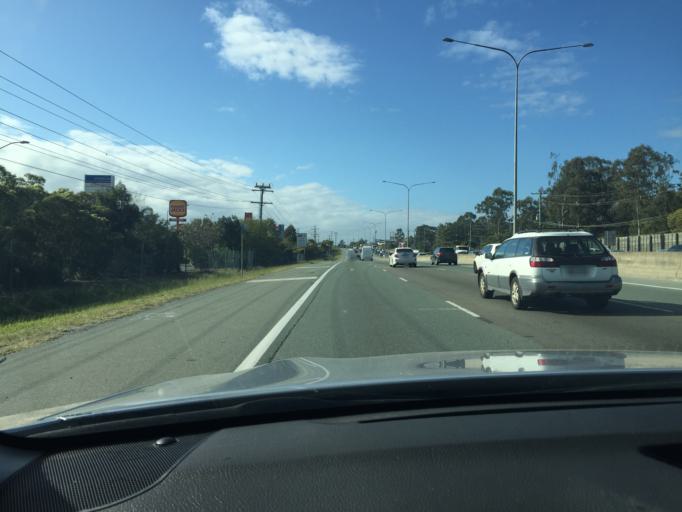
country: AU
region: Queensland
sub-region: Logan
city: Slacks Creek
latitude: -27.6579
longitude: 153.1670
